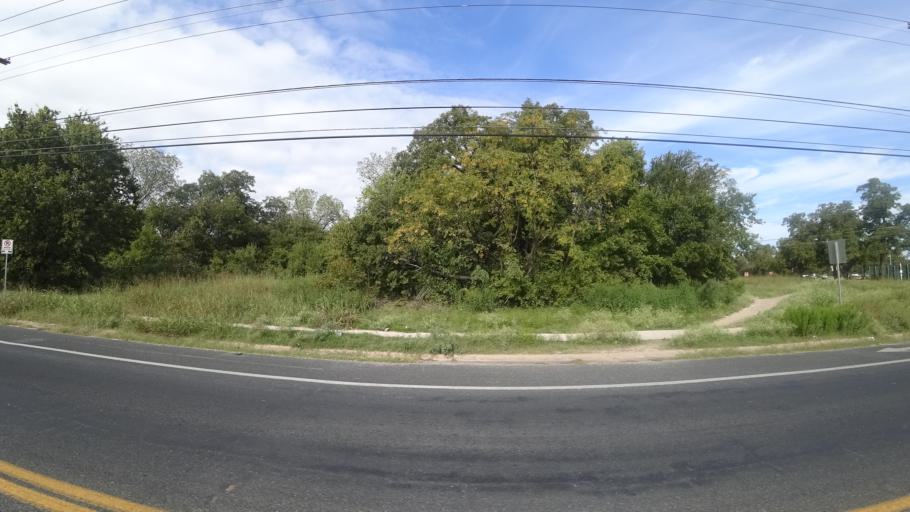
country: US
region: Texas
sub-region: Travis County
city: Austin
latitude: 30.2729
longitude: -97.6908
